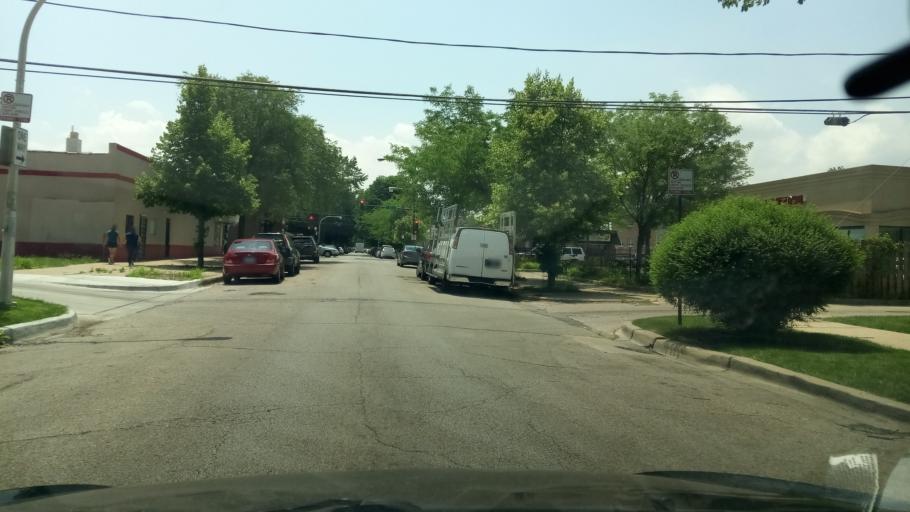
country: US
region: Illinois
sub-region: Cook County
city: Hometown
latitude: 41.7794
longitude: -87.7275
